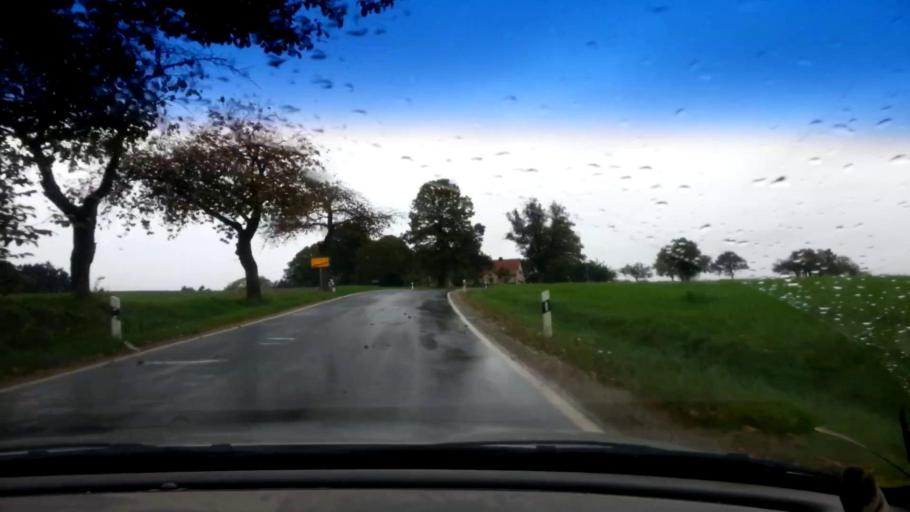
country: DE
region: Bavaria
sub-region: Upper Franconia
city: Poxdorf
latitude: 49.9390
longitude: 11.0793
